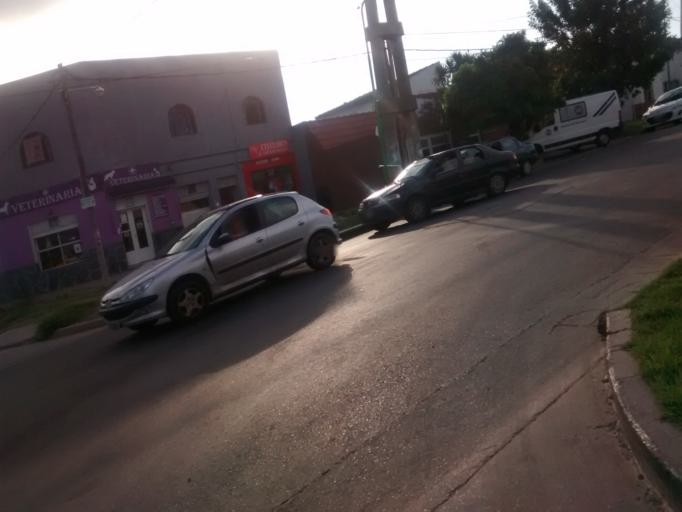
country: AR
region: Buenos Aires
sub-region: Partido de La Plata
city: La Plata
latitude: -34.9427
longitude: -57.9258
